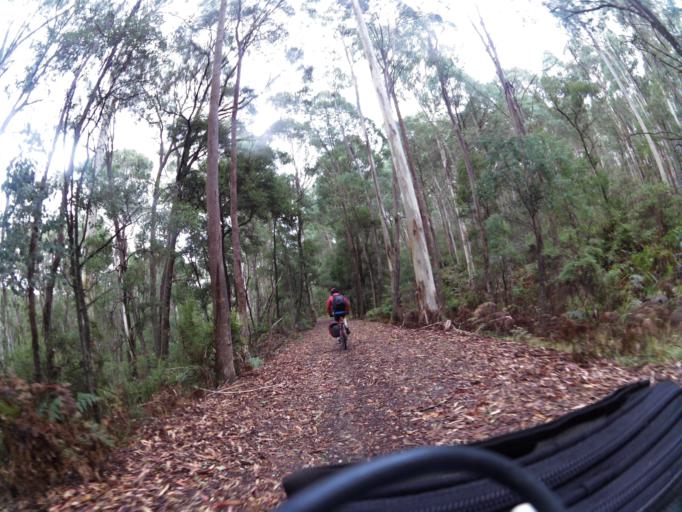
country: AU
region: New South Wales
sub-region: Greater Hume Shire
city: Holbrook
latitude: -36.1681
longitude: 147.4900
